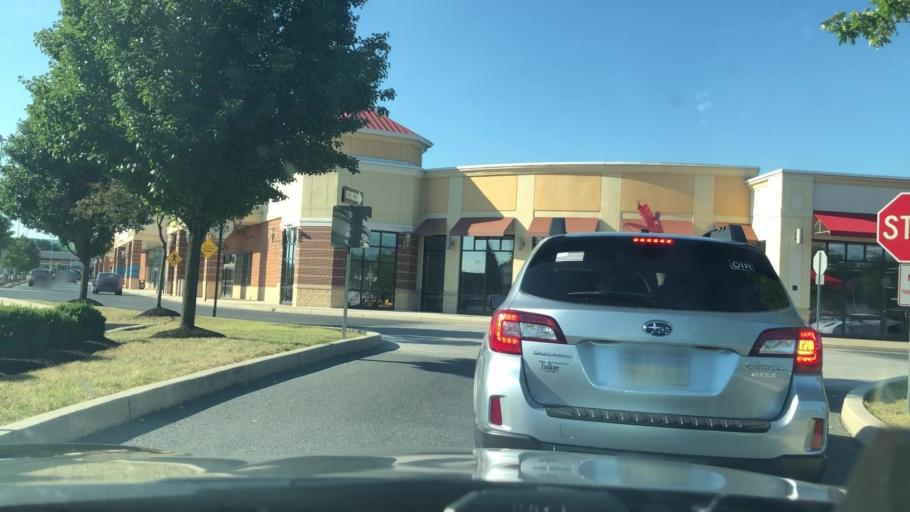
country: US
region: Pennsylvania
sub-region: Cumberland County
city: Mechanicsburg
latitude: 40.2472
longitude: -77.0074
